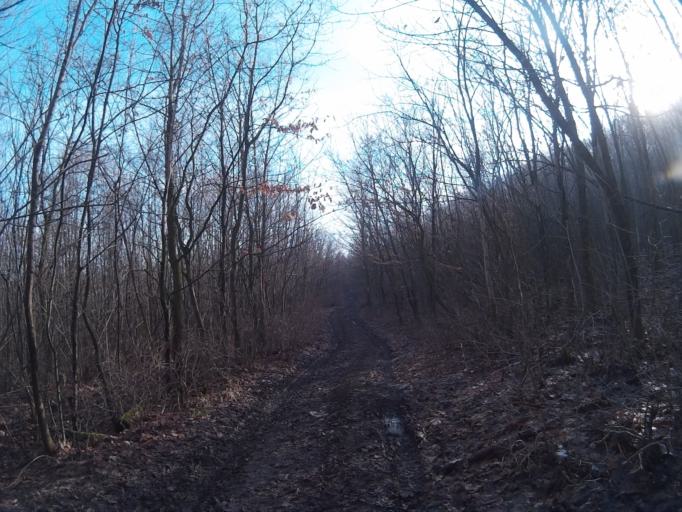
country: HU
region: Komarom-Esztergom
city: Tarjan
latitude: 47.6186
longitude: 18.4745
